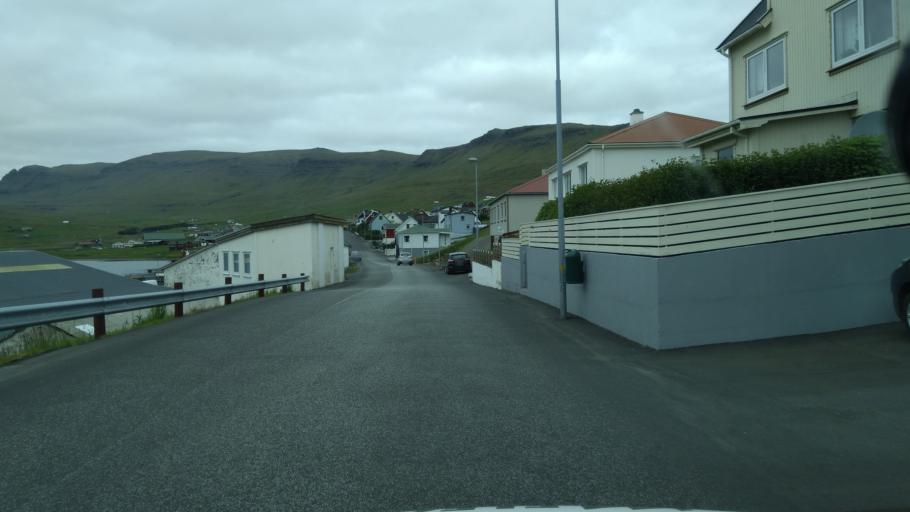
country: FO
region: Suduroy
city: Tvoroyri
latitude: 61.5617
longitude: -6.8285
